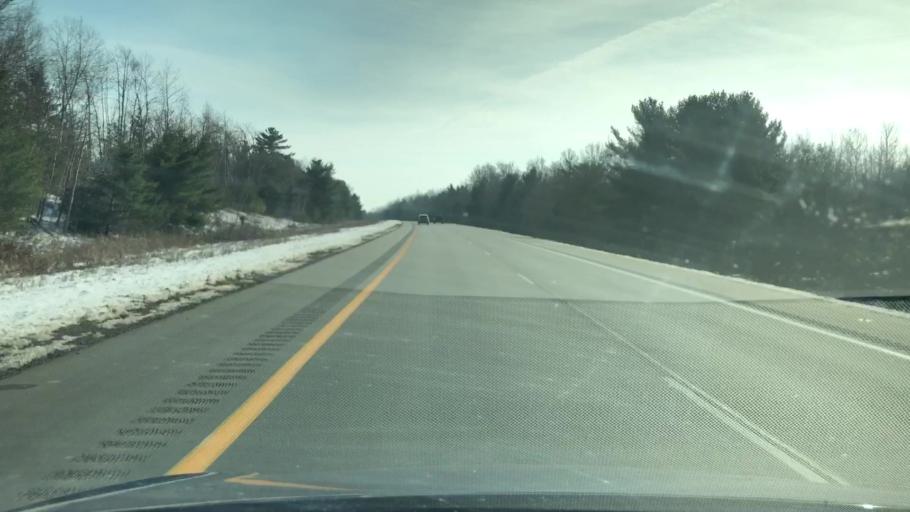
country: US
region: Michigan
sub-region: Ogemaw County
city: Skidway Lake
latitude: 44.0685
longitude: -84.0904
